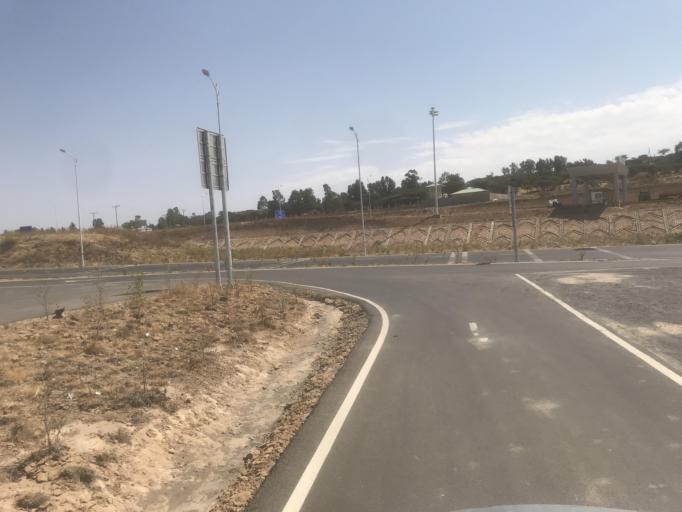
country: ET
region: Oromiya
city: Mojo
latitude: 8.5674
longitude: 39.1631
